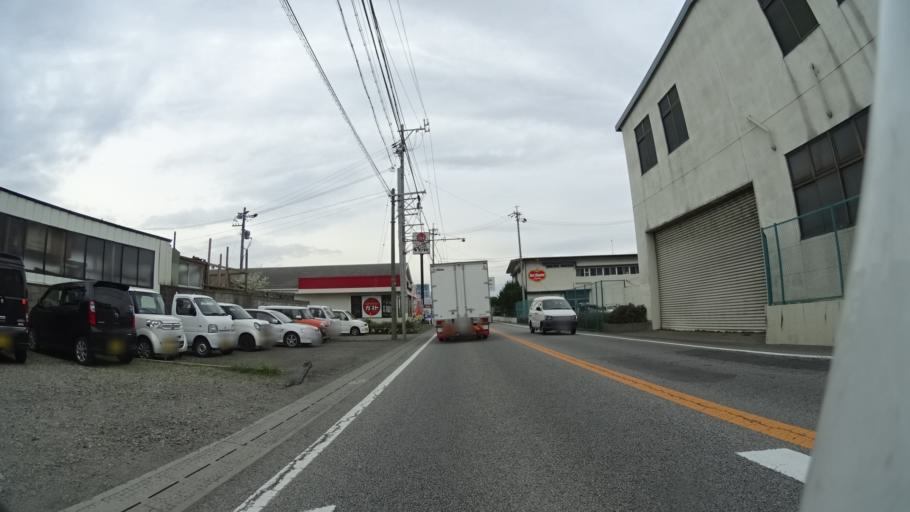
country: JP
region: Nagano
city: Nagano-shi
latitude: 36.5321
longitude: 138.1232
